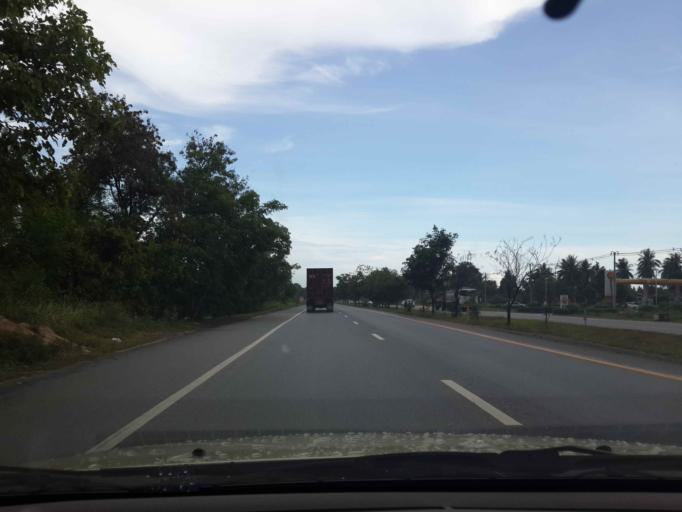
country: TH
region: Chon Buri
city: Phatthaya
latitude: 12.9422
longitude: 100.9942
